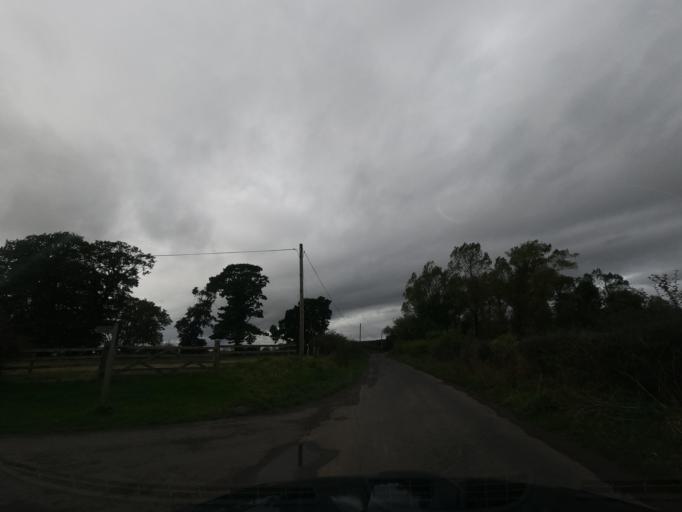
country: GB
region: England
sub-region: Northumberland
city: Doddington
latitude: 55.5971
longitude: -2.0261
